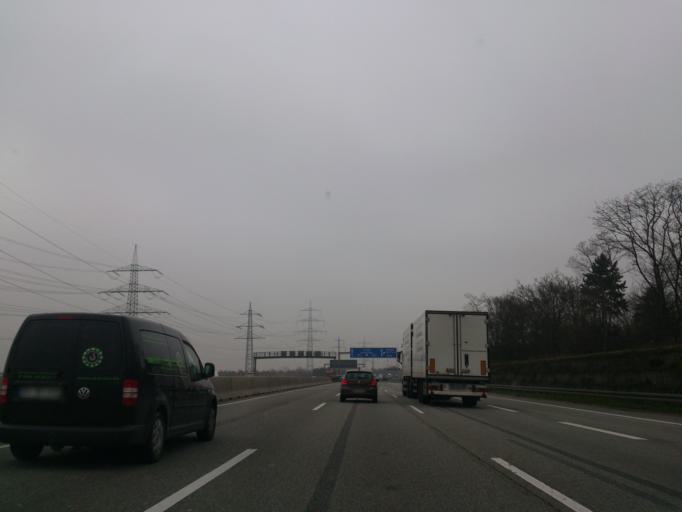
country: DE
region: North Rhine-Westphalia
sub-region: Regierungsbezirk Dusseldorf
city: Neuss
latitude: 51.1893
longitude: 6.6606
